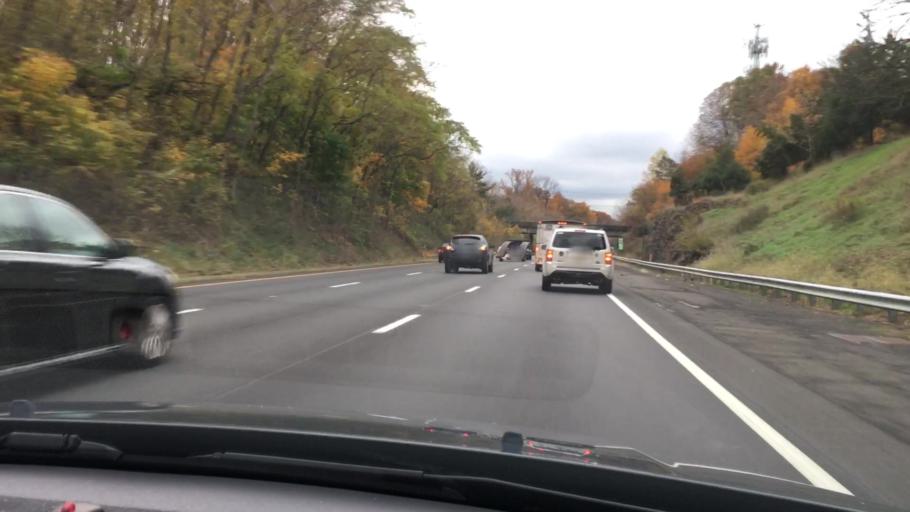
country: US
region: New Jersey
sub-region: Somerset County
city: Bedminster
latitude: 40.6743
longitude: -74.6106
